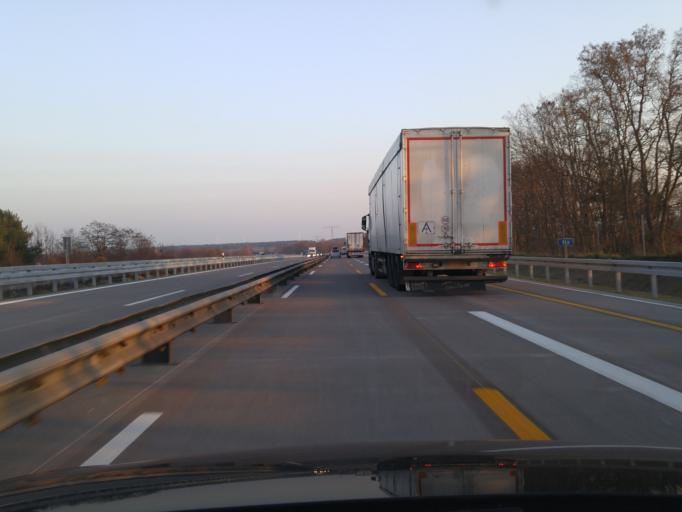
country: DE
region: Brandenburg
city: Golzow
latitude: 52.3378
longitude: 12.6485
